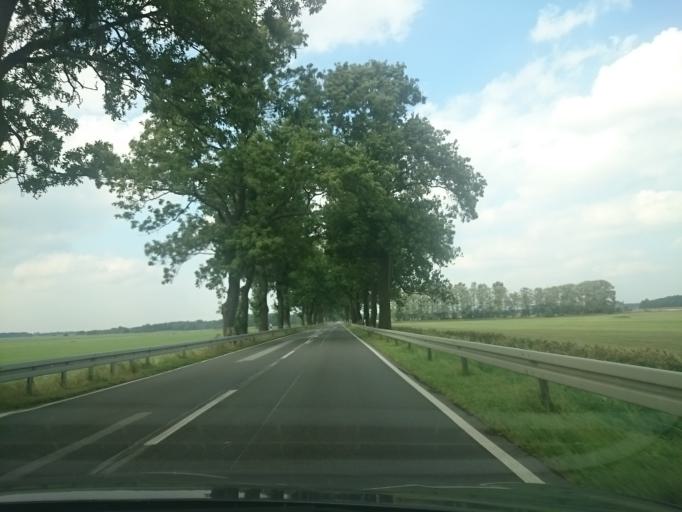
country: DE
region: Mecklenburg-Vorpommern
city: Ferdinandshof
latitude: 53.6794
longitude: 13.8841
